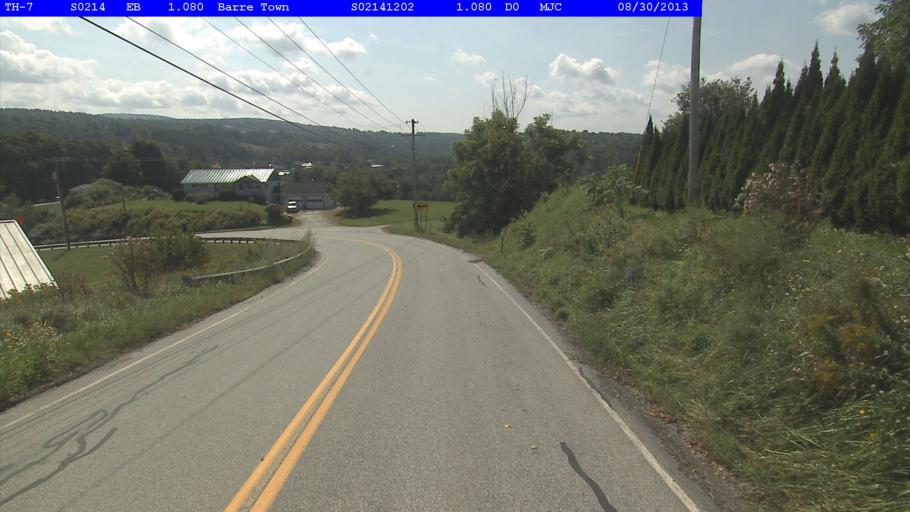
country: US
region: Vermont
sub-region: Washington County
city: South Barre
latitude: 44.1788
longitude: -72.5100
